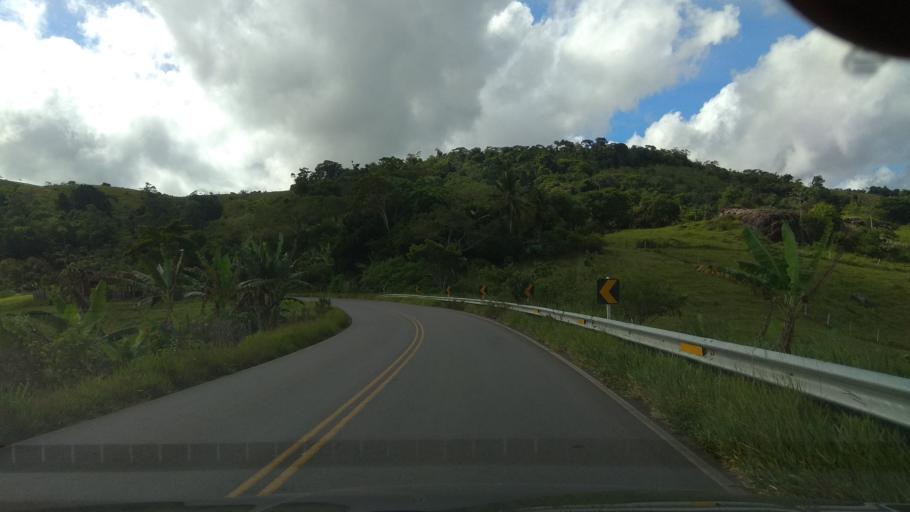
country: BR
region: Bahia
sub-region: Mutuipe
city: Mutuipe
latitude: -13.1912
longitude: -39.4444
